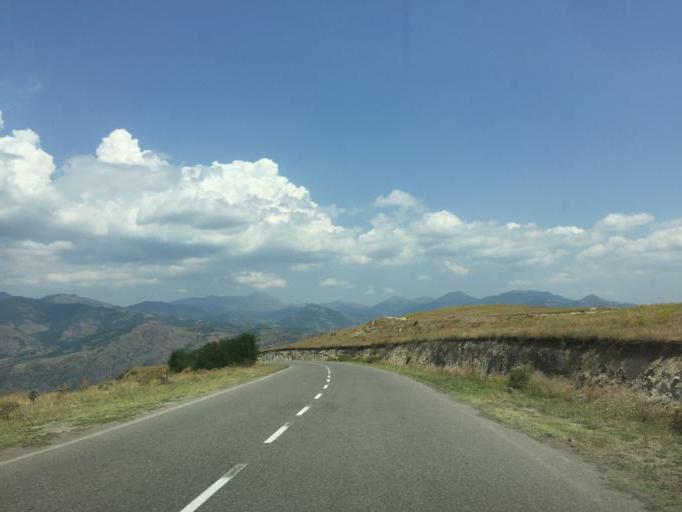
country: AZ
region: Lacin
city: Lacin
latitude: 39.5861
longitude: 46.5230
